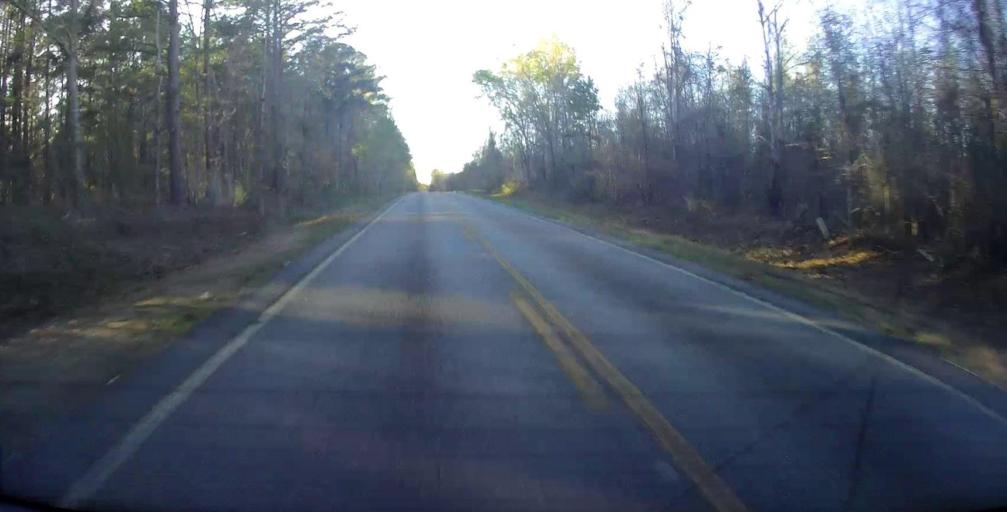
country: US
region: Georgia
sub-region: Wilcox County
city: Abbeville
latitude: 32.1053
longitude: -83.3096
